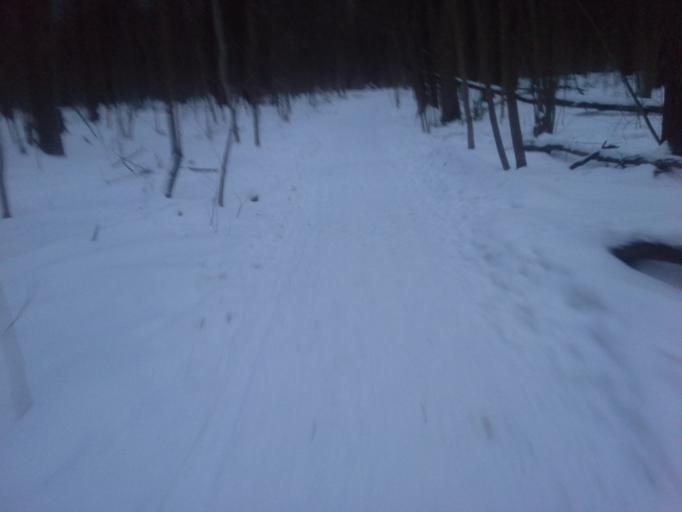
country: RU
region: Moscow
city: Yasenevo
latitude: 55.5644
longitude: 37.5379
